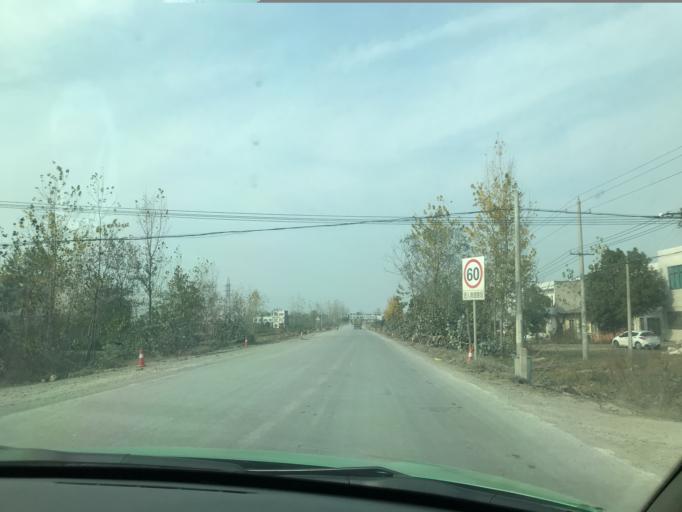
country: CN
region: Hubei
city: Tianmen
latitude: 30.7050
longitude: 113.1240
